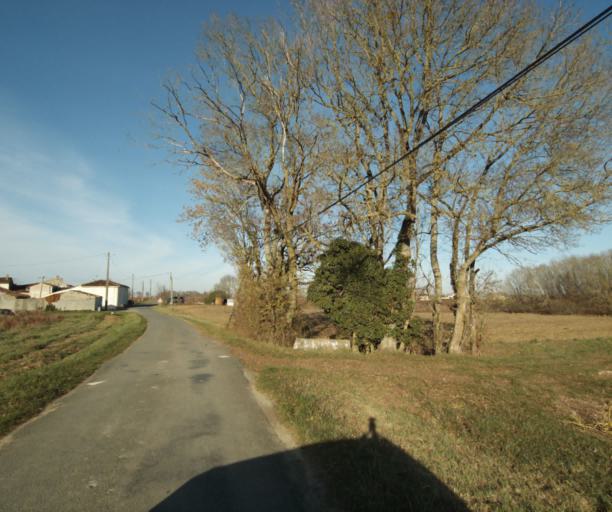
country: FR
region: Poitou-Charentes
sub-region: Departement de la Charente-Maritime
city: Burie
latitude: 45.7837
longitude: -0.4171
